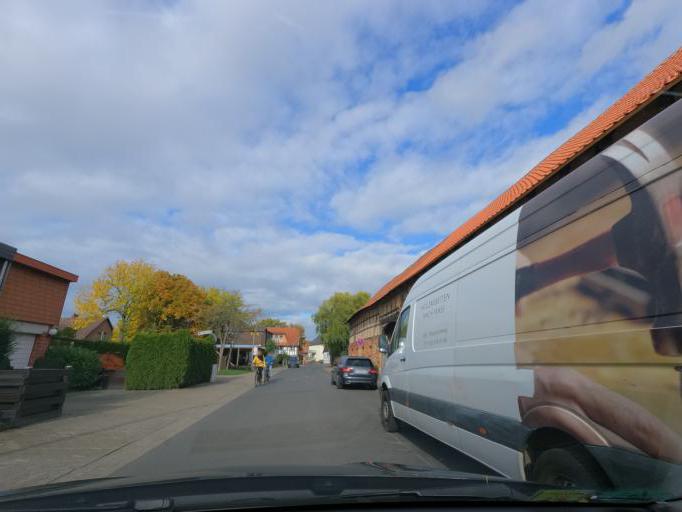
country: DE
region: Lower Saxony
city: Leiferde
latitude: 52.2081
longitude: 10.5224
